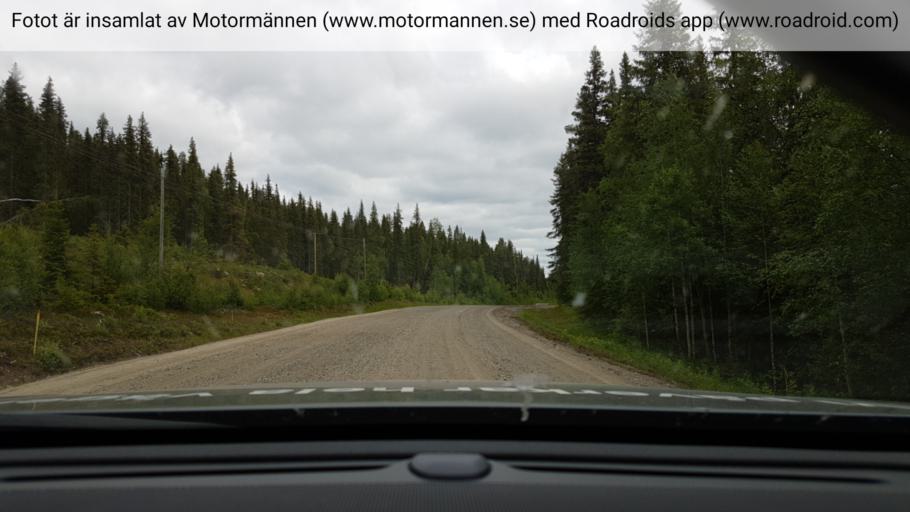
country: SE
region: Vaesterbotten
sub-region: Storumans Kommun
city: Fristad
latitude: 65.8186
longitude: 16.7962
